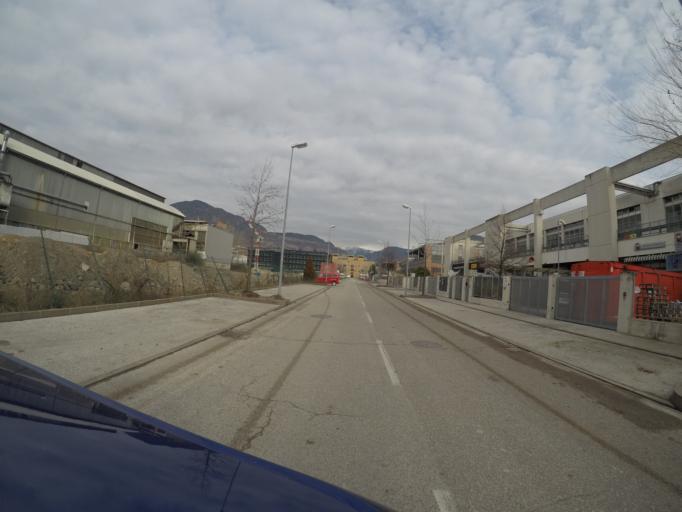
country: IT
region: Trentino-Alto Adige
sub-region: Bolzano
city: Bolzano
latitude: 46.4758
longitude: 11.3314
